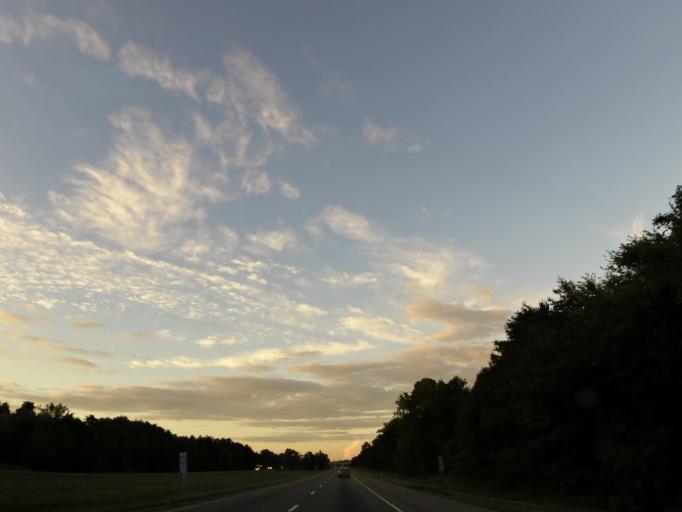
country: US
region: Tennessee
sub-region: McMinn County
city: Athens
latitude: 35.5354
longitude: -84.5790
